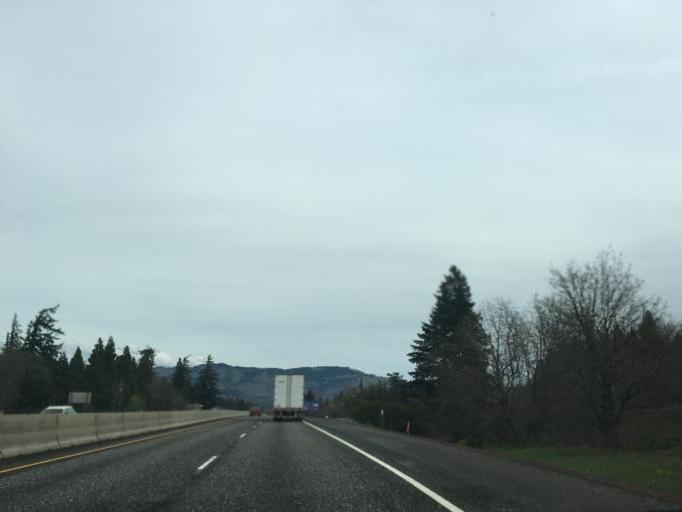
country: US
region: Oregon
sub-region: Hood River County
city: Hood River
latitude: 45.7083
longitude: -121.5640
